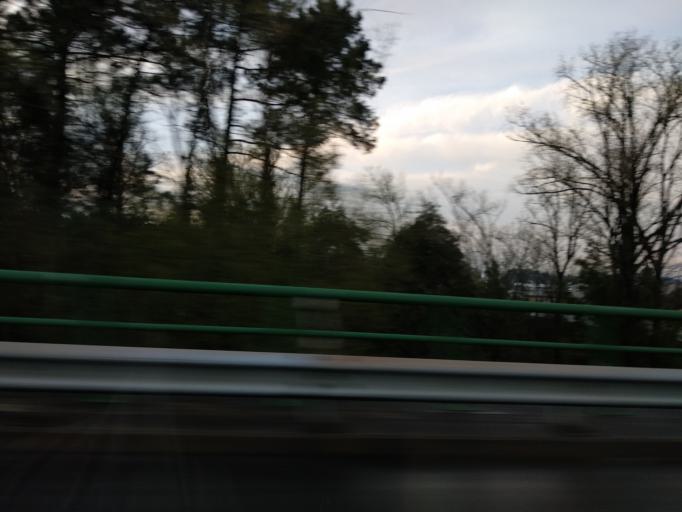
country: PT
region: Braga
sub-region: Braga
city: Oliveira
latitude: 41.5078
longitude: -8.4579
